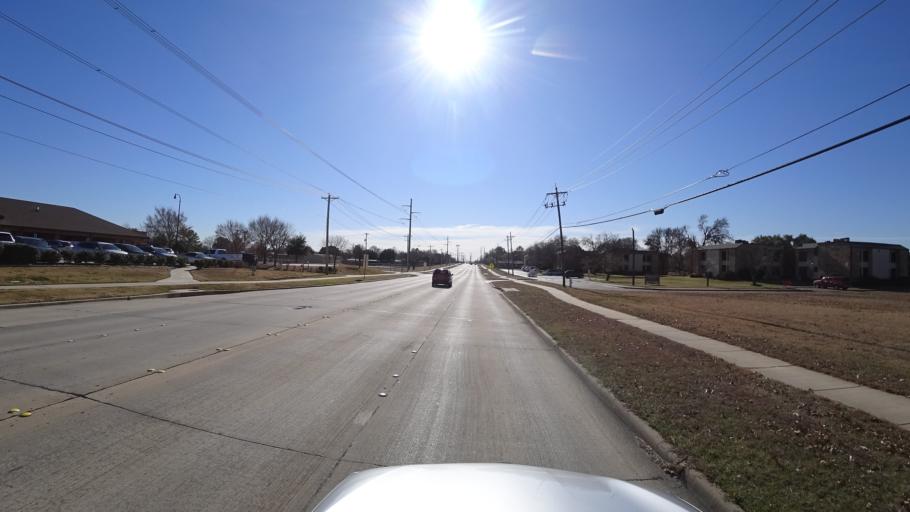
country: US
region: Texas
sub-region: Denton County
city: Lewisville
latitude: 33.0338
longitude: -97.0104
